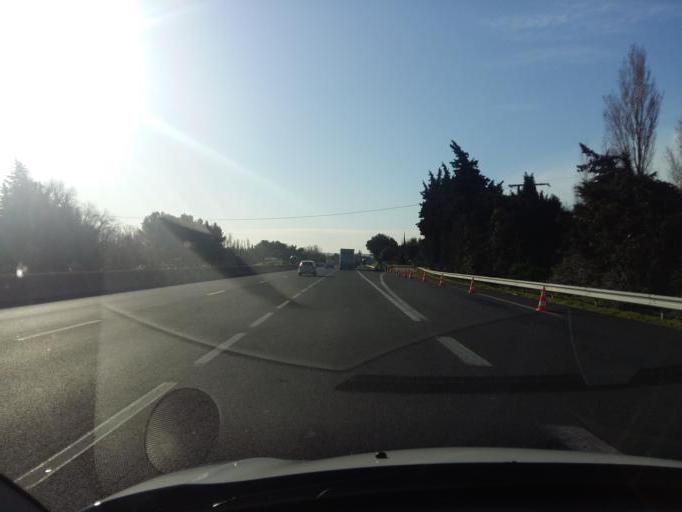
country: FR
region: Provence-Alpes-Cote d'Azur
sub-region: Departement des Bouches-du-Rhone
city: Senas
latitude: 43.7396
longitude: 5.0816
